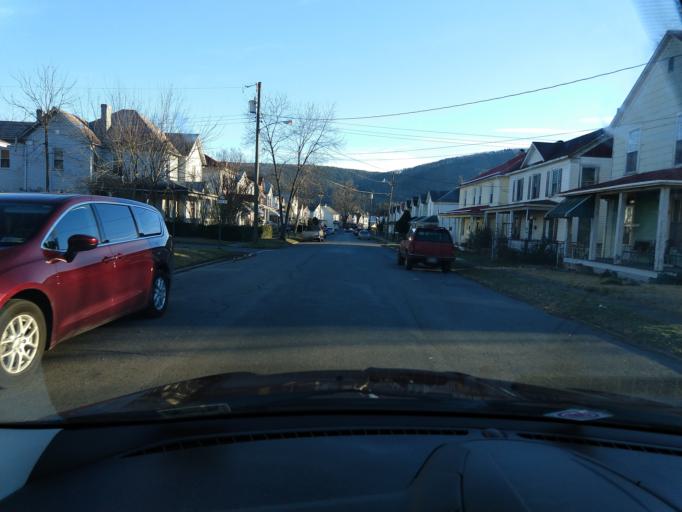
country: US
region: Virginia
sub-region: Alleghany County
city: Clifton Forge
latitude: 37.8224
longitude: -79.8290
